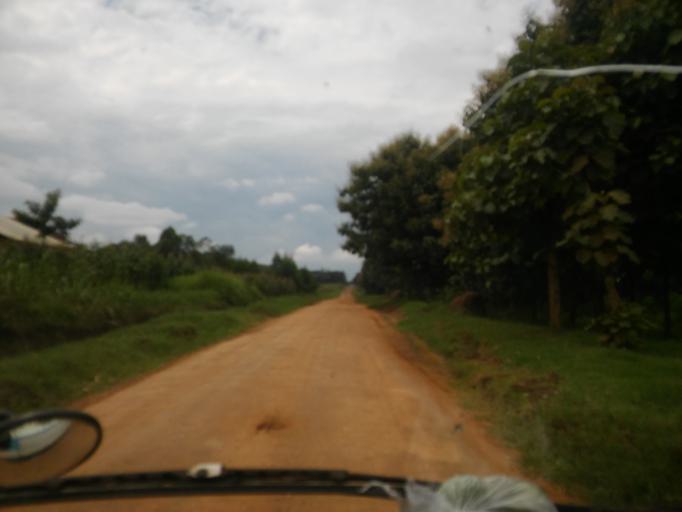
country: UG
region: Eastern Region
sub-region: Bududa District
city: Bududa
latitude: 0.9453
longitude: 34.2337
